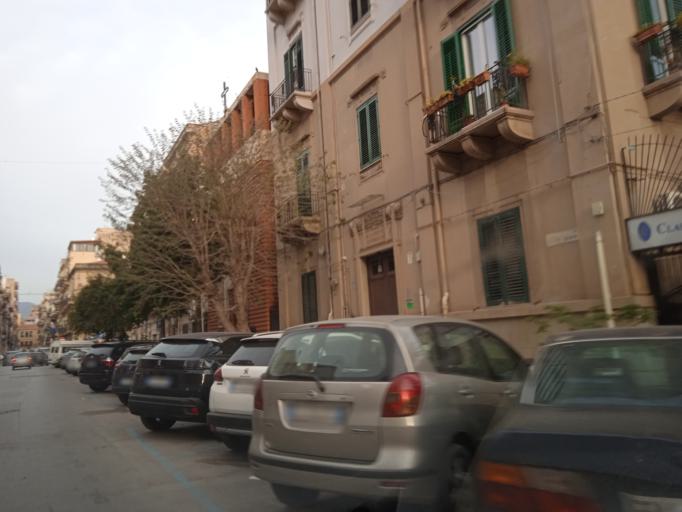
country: IT
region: Sicily
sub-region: Palermo
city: Palermo
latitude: 38.1210
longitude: 13.3485
